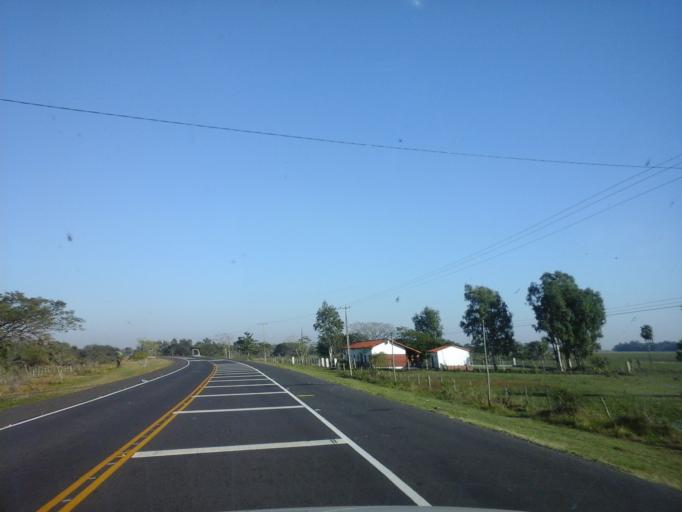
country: PY
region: Neembucu
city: Pilar
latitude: -26.8650
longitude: -58.1327
